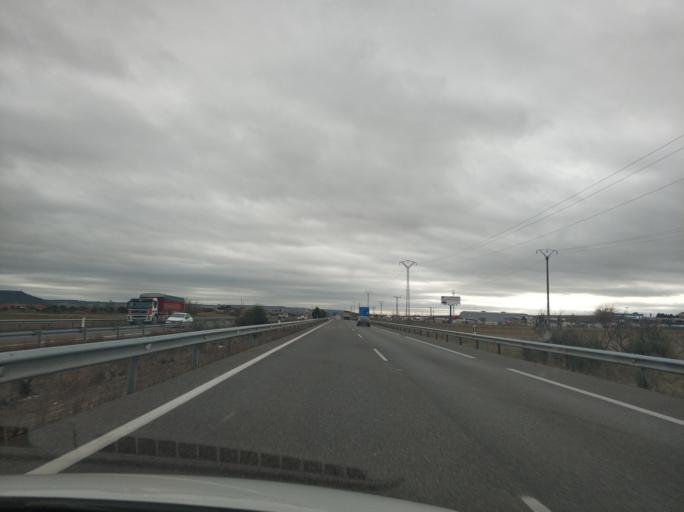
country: ES
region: Castille and Leon
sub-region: Provincia de Valladolid
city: Cubillas de Santa Marta
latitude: 41.8230
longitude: -4.5770
